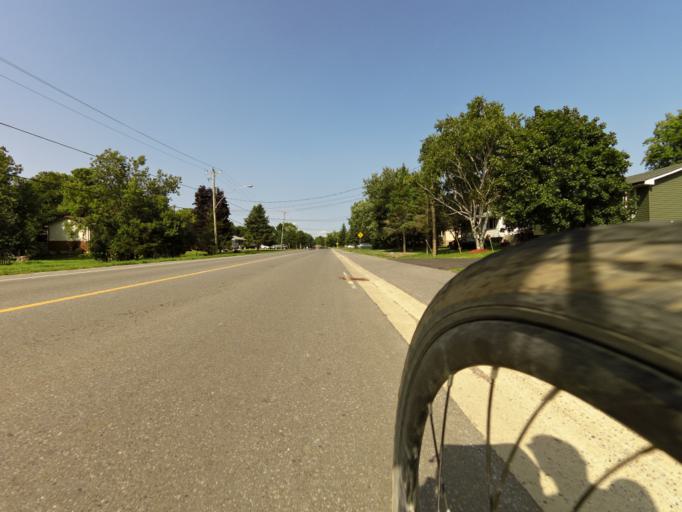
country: CA
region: Ontario
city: Skatepark
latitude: 44.2725
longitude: -76.7157
